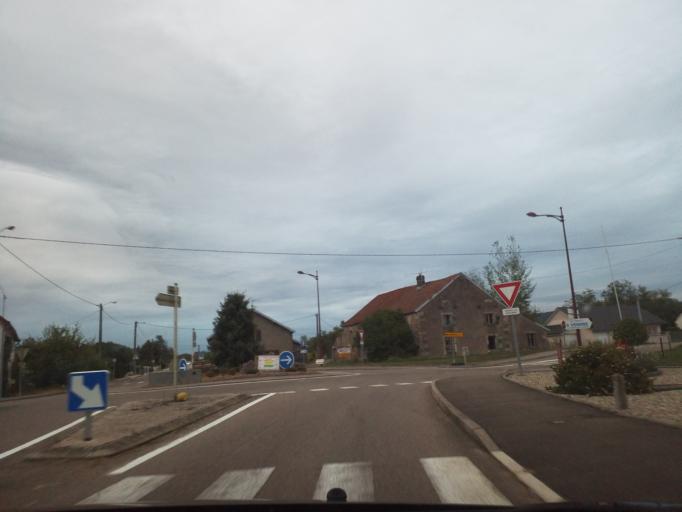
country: FR
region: Franche-Comte
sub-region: Departement de la Haute-Saone
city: Saint-Germain
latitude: 47.7264
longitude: 6.5371
